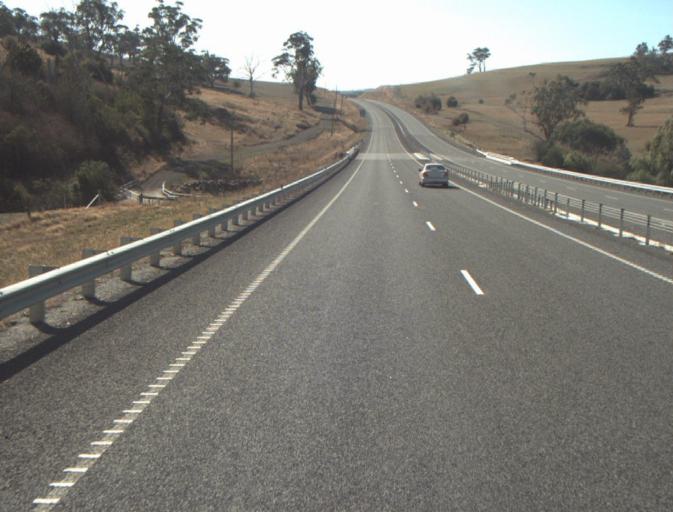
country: AU
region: Tasmania
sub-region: Launceston
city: Mayfield
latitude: -41.3630
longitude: 147.1074
